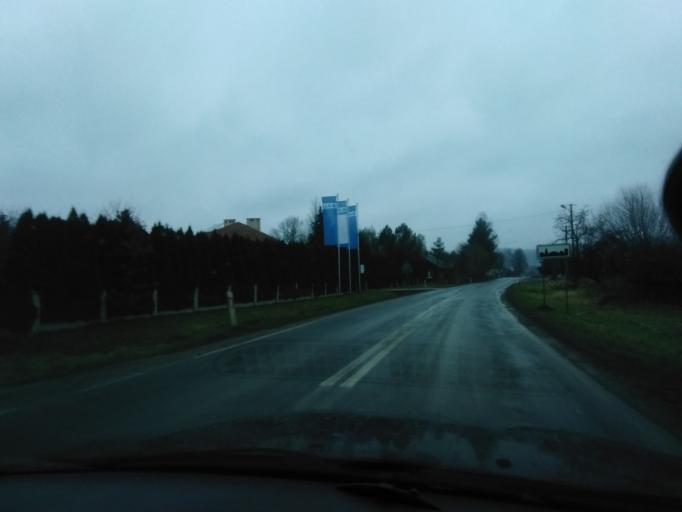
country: PL
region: Subcarpathian Voivodeship
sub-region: Powiat strzyzowski
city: Strzyzow
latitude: 49.8285
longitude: 21.8270
